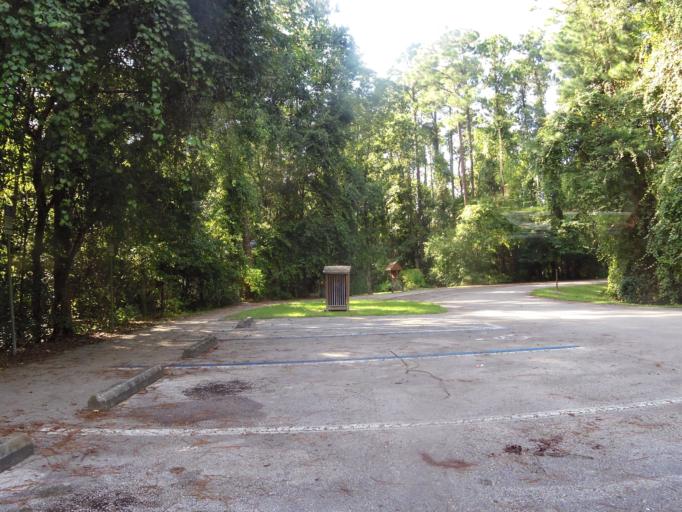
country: US
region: Florida
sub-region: Clay County
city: Orange Park
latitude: 30.2381
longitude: -81.6993
